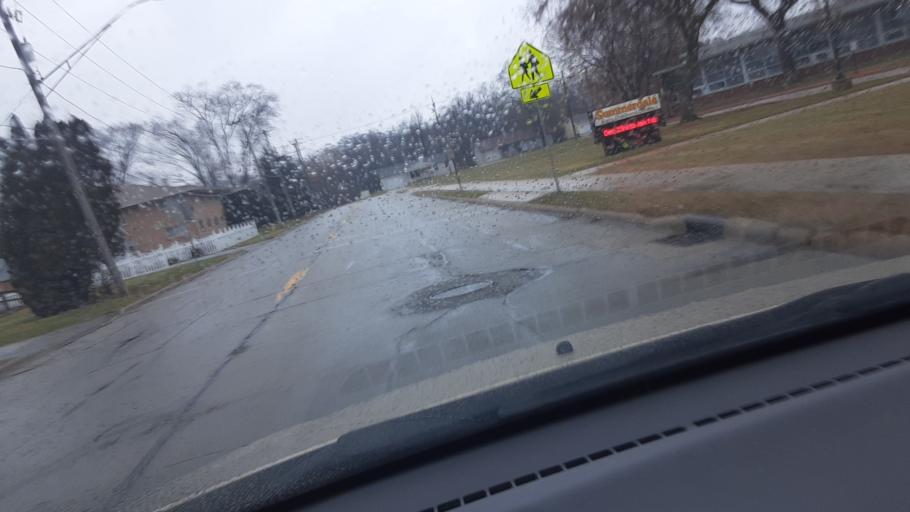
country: US
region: Illinois
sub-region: Winnebago County
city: Rockford
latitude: 42.3000
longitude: -89.1064
